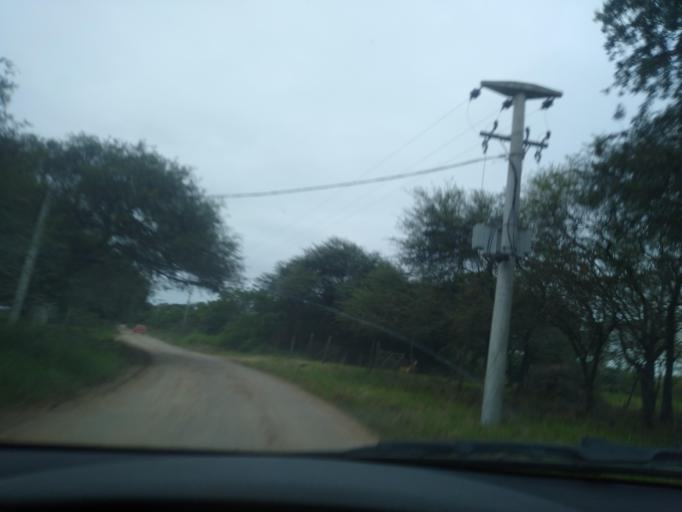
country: AR
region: Chaco
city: Colonia Benitez
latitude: -27.3357
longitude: -58.9619
